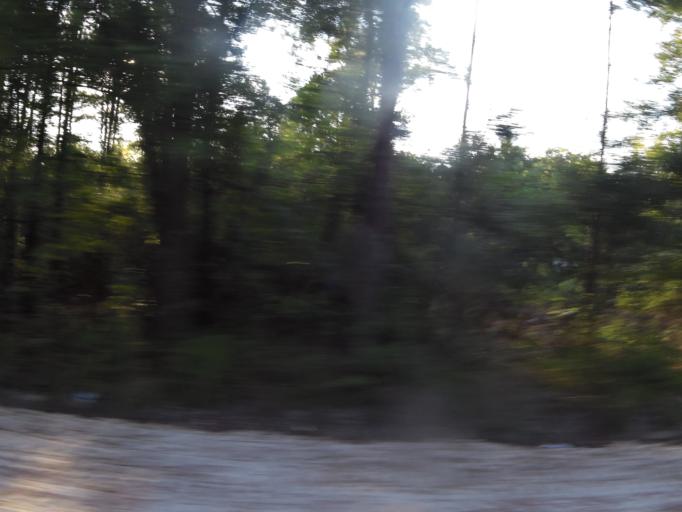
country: US
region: Florida
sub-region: Nassau County
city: Hilliard
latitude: 30.5508
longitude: -81.9947
